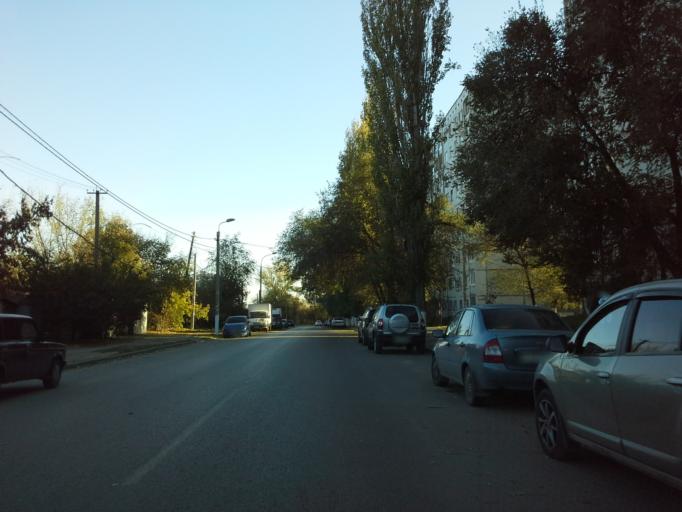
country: RU
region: Volgograd
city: Vodstroy
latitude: 48.8175
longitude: 44.6358
